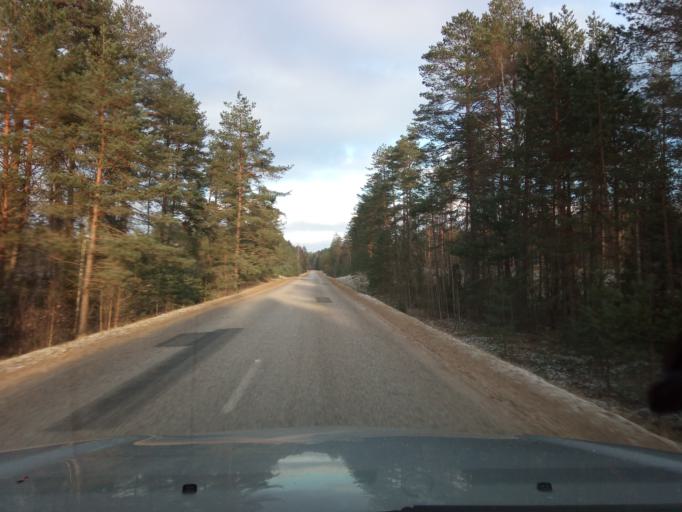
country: LT
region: Alytaus apskritis
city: Varena
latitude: 54.0983
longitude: 24.4250
